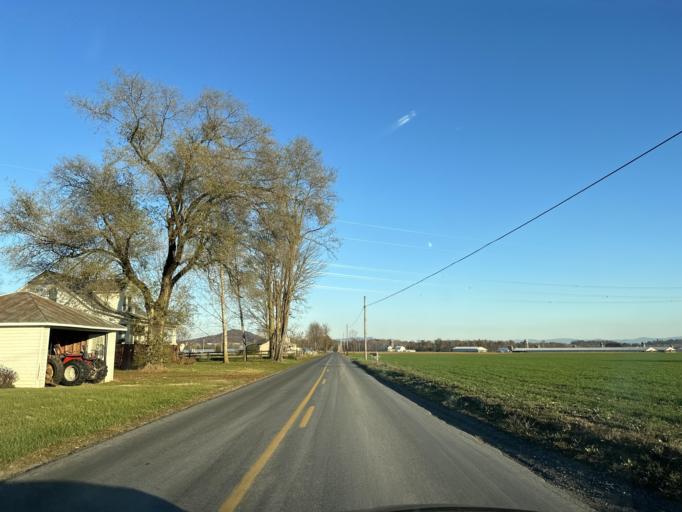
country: US
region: Virginia
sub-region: Rockingham County
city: Bridgewater
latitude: 38.4484
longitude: -79.0057
